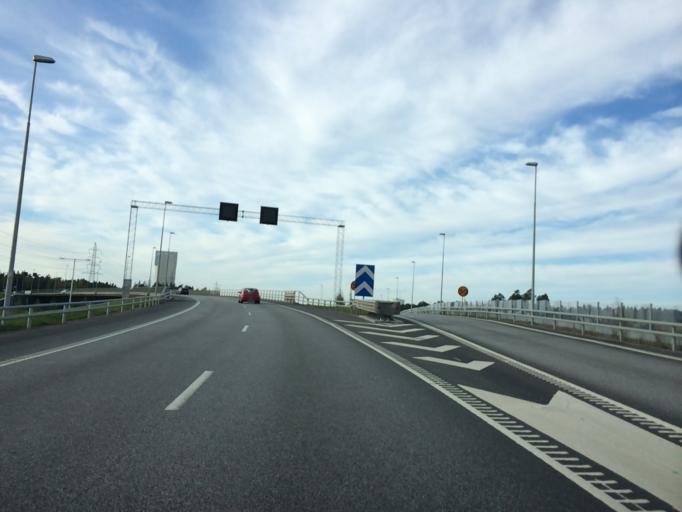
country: SE
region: Stockholm
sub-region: Stockholms Kommun
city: Kista
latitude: 59.4009
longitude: 17.9756
